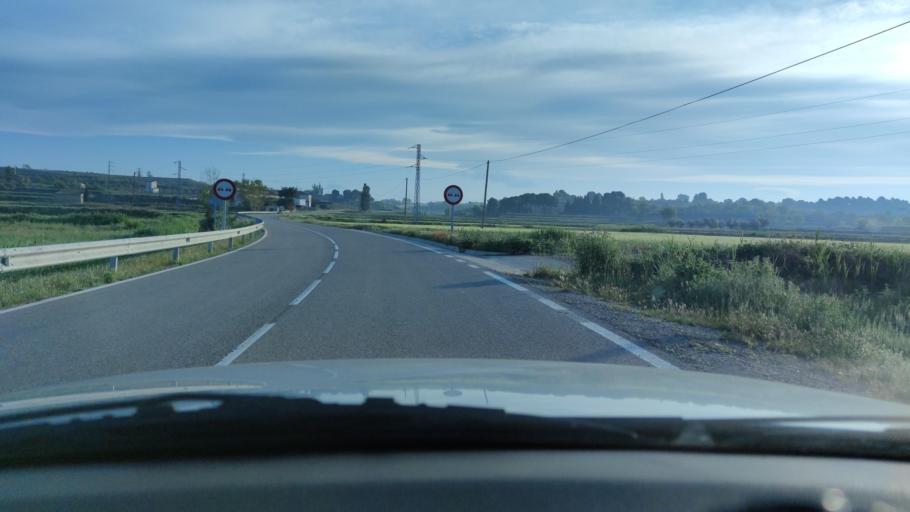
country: ES
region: Catalonia
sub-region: Provincia de Lleida
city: Castellsera
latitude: 41.7554
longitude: 0.9947
